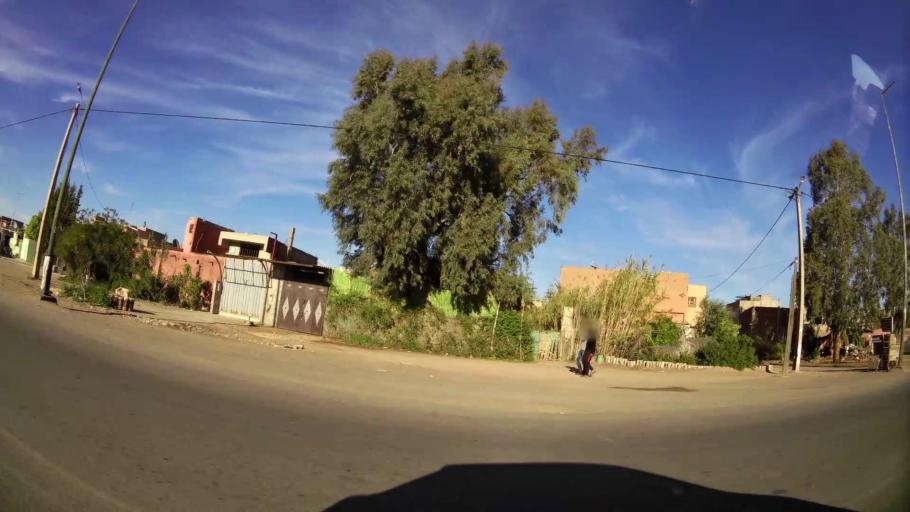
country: MA
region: Marrakech-Tensift-Al Haouz
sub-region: Marrakech
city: Marrakesh
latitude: 31.6776
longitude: -8.0594
